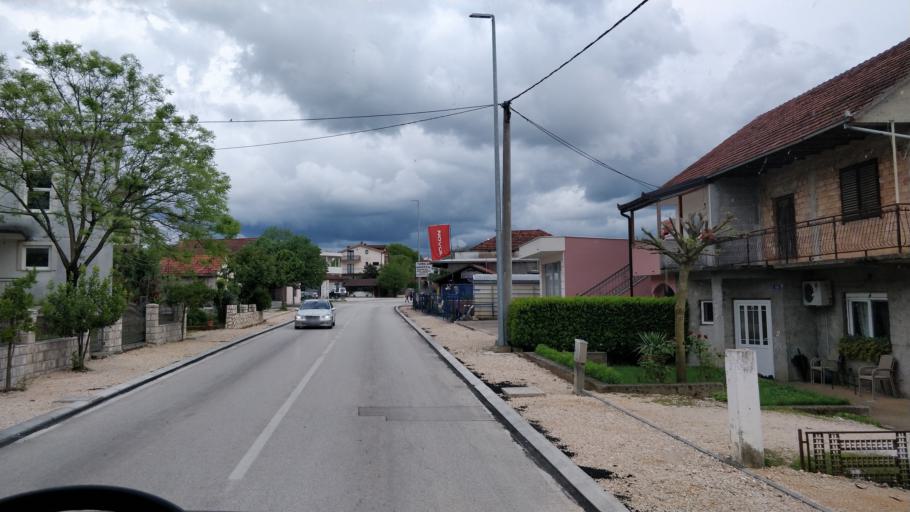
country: BA
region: Federation of Bosnia and Herzegovina
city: Ljubuski
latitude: 43.1897
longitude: 17.5361
